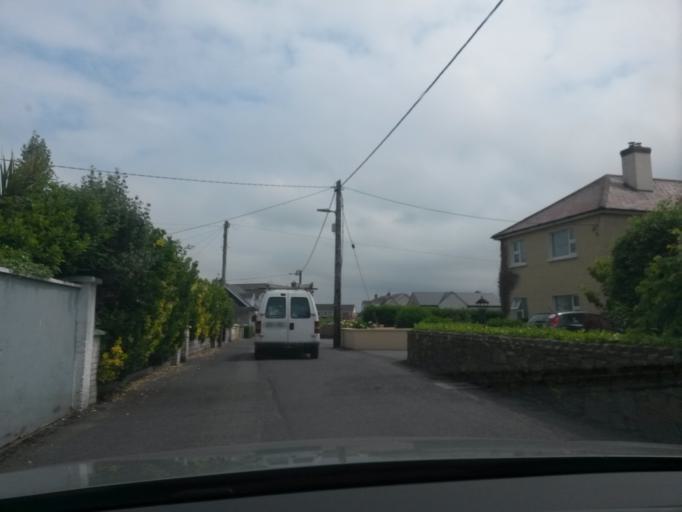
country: IE
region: Munster
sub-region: Ciarrai
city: Ballybunnion
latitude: 52.5109
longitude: -9.6725
